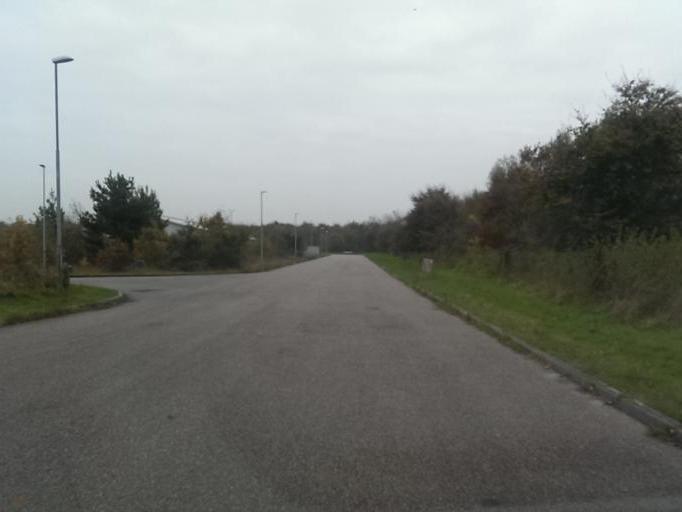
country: DK
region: South Denmark
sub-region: Esbjerg Kommune
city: Esbjerg
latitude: 55.5047
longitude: 8.4605
